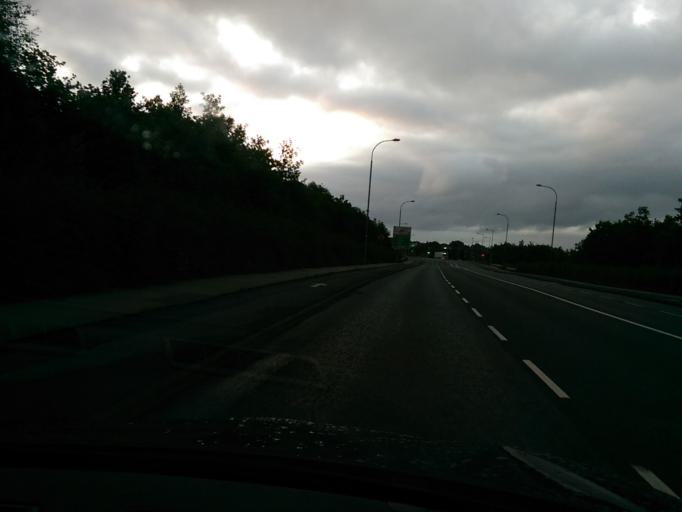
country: IE
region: Connaught
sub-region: County Galway
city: Gaillimh
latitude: 53.2828
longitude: -9.0523
